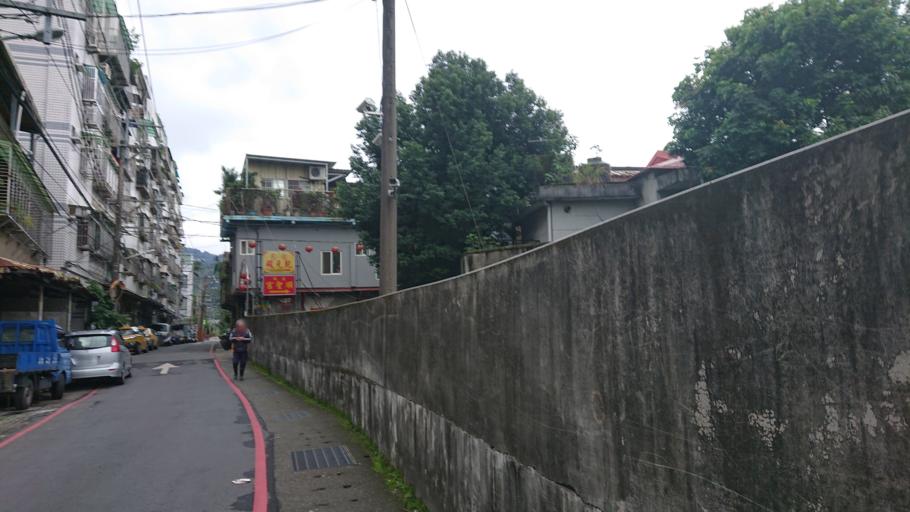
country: TW
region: Taipei
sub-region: Taipei
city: Banqiao
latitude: 24.9629
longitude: 121.4402
